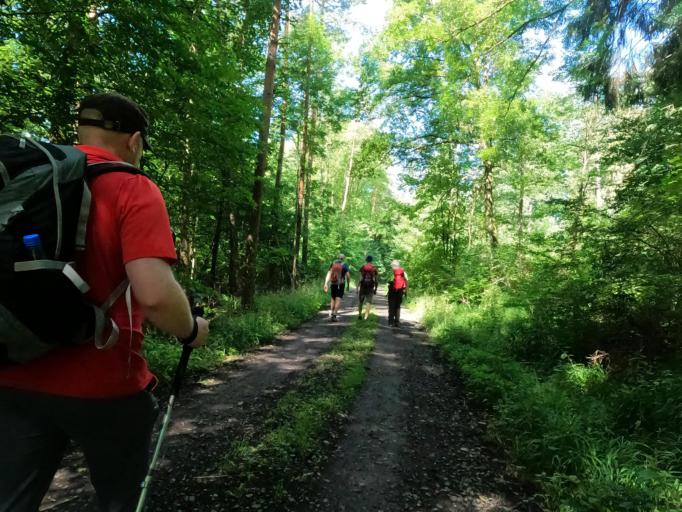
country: DE
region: Bavaria
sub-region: Regierungsbezirk Unterfranken
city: Zeitlofs
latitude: 50.3325
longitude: 9.6361
